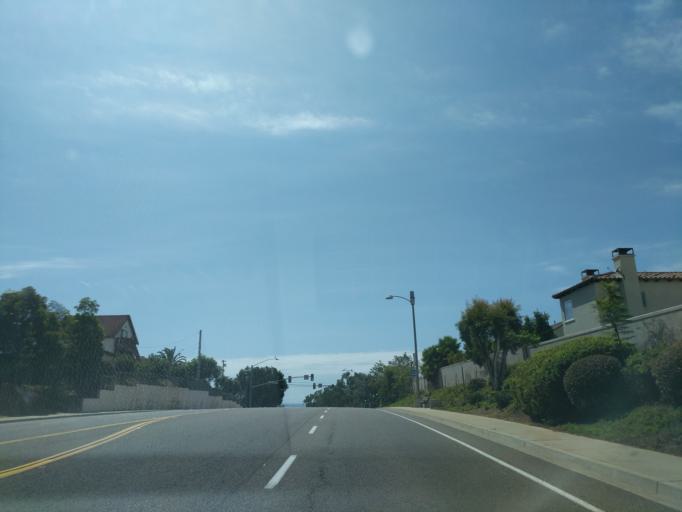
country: US
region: California
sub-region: San Diego County
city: Carlsbad
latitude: 33.1667
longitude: -117.3369
